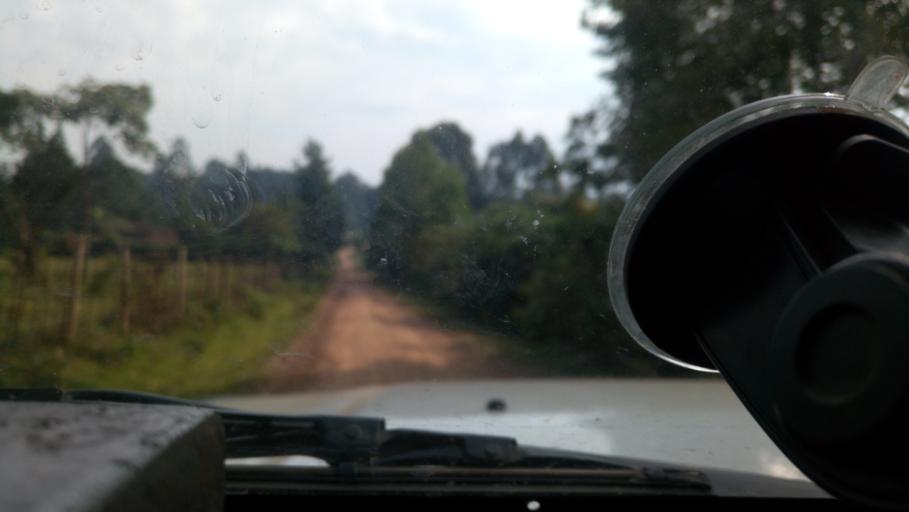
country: KE
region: Kericho
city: Litein
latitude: -0.5746
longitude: 35.1889
